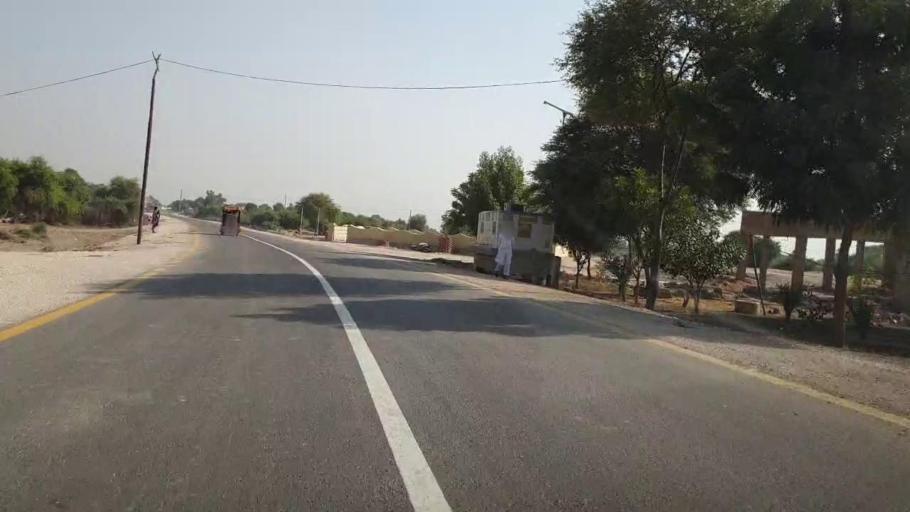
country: PK
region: Sindh
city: Bhan
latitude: 26.5660
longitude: 67.7697
